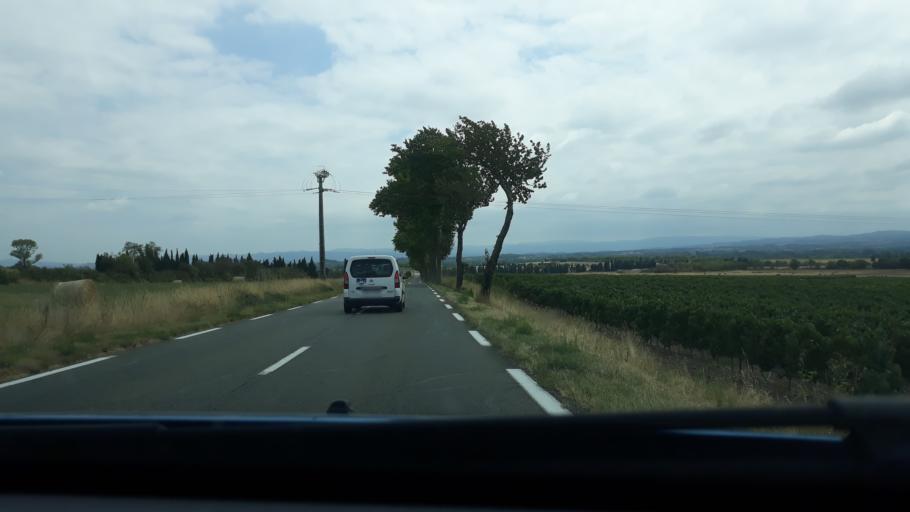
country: FR
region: Languedoc-Roussillon
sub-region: Departement de l'Aude
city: Pezens
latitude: 43.2723
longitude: 2.2356
